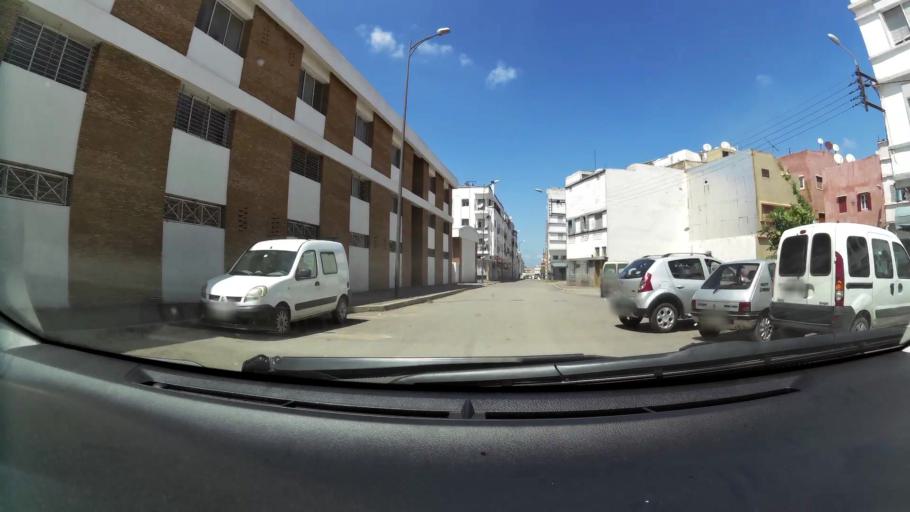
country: MA
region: Grand Casablanca
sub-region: Casablanca
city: Casablanca
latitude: 33.5583
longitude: -7.5834
